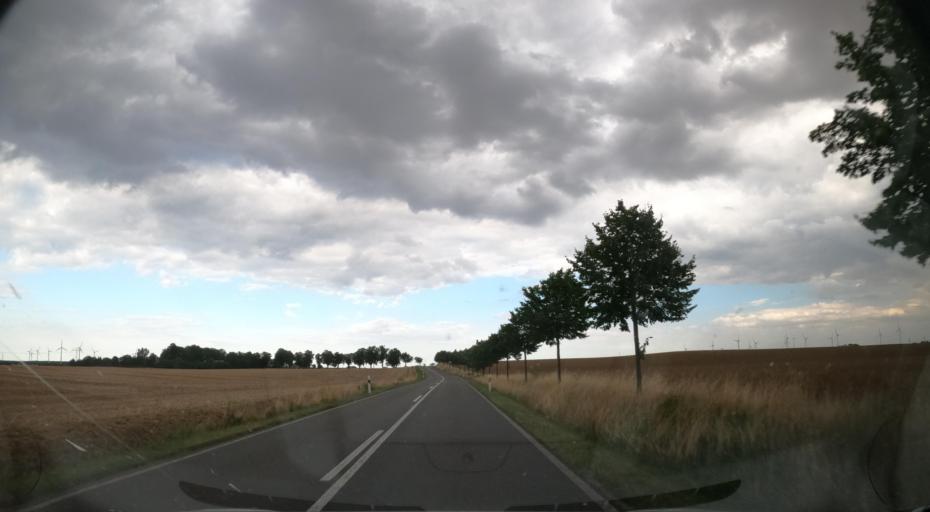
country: DE
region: Mecklenburg-Vorpommern
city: Strasburg
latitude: 53.4909
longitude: 13.8209
